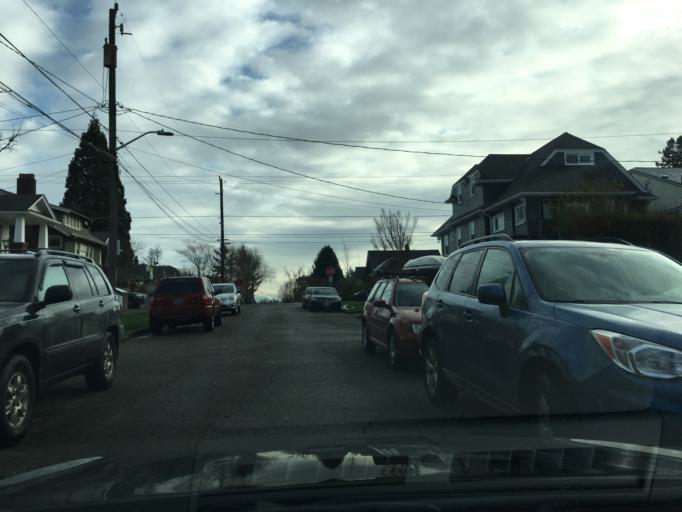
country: US
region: Washington
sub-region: King County
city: Seattle
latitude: 47.6672
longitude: -122.3264
